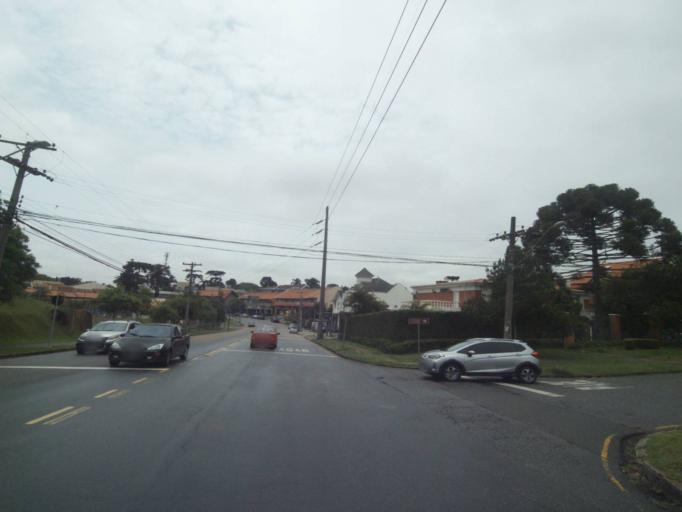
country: BR
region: Parana
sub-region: Curitiba
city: Curitiba
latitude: -25.4070
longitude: -49.2829
